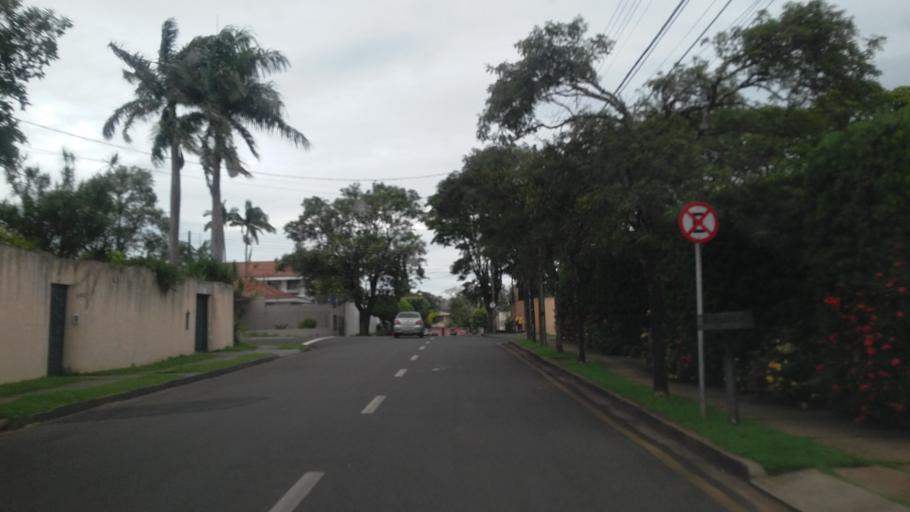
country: BR
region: Parana
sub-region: Londrina
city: Londrina
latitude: -23.3116
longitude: -51.1789
